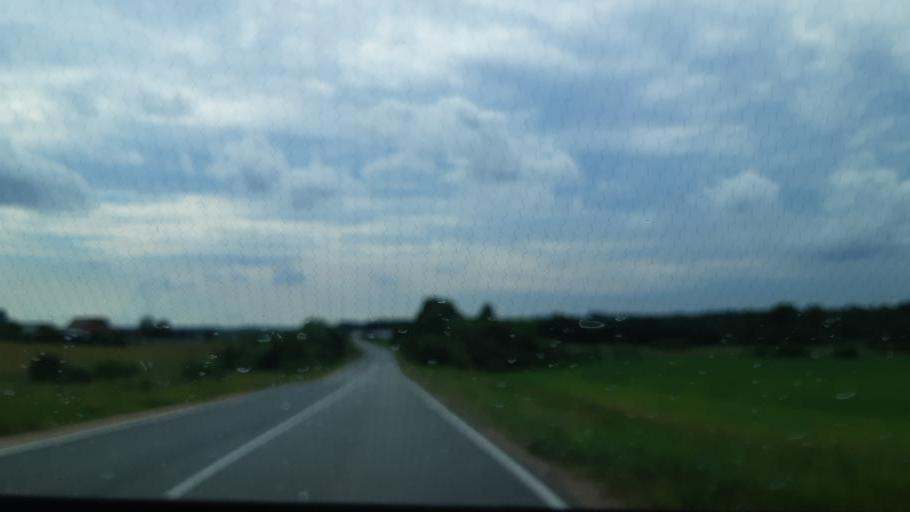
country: RU
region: Moskovskaya
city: Vereya
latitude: 55.2099
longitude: 35.9987
